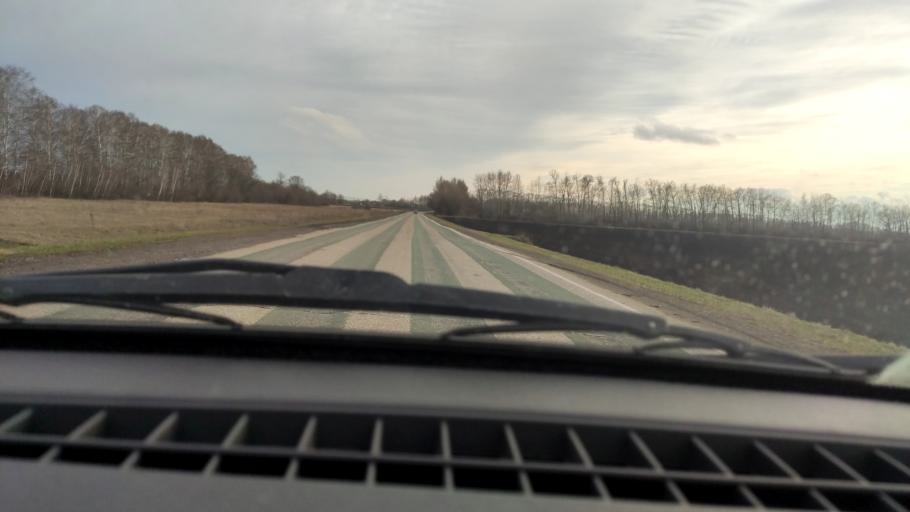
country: RU
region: Bashkortostan
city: Chishmy
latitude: 54.4571
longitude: 55.2535
